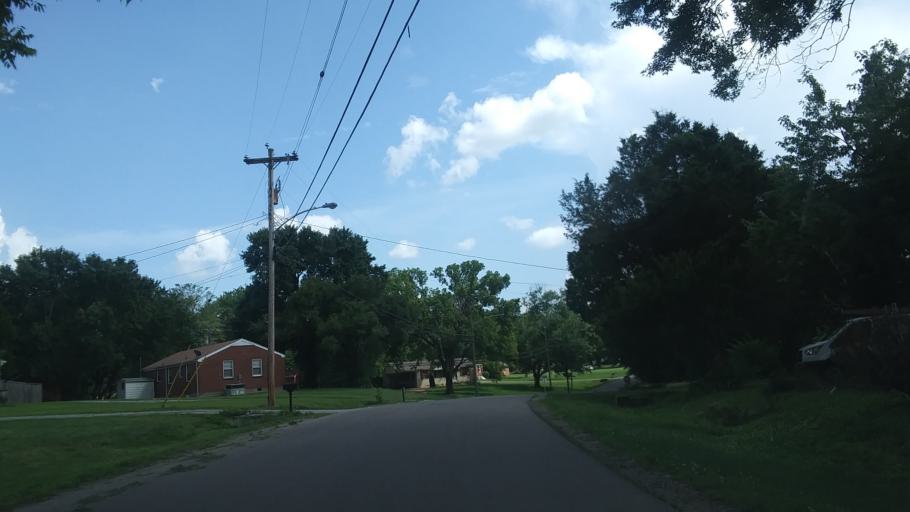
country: US
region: Tennessee
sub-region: Davidson County
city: Oak Hill
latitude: 36.0646
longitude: -86.7144
